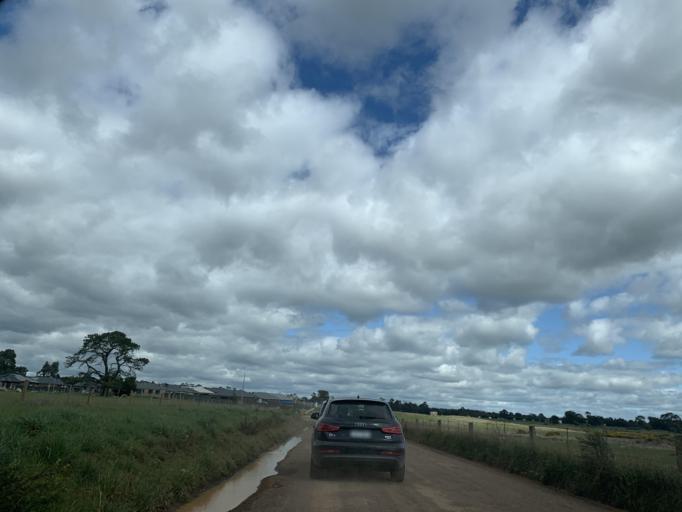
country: AU
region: Victoria
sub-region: Whittlesea
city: Whittlesea
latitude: -37.2852
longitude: 144.9296
